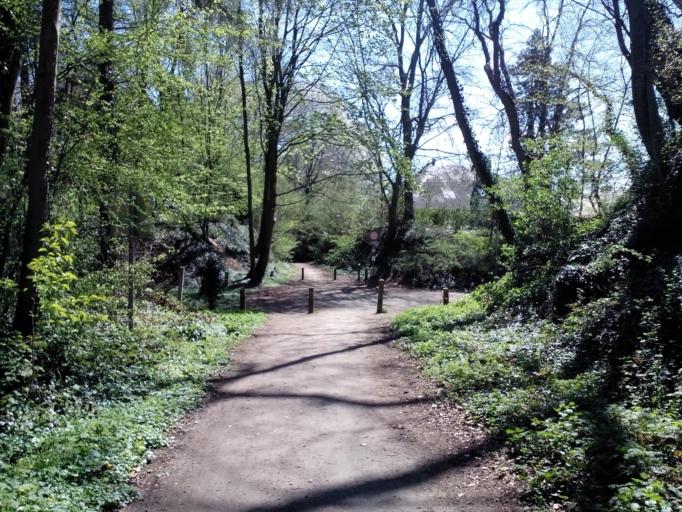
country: BE
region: Flanders
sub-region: Provincie Vlaams-Brabant
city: Tervuren
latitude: 50.8356
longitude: 4.5408
